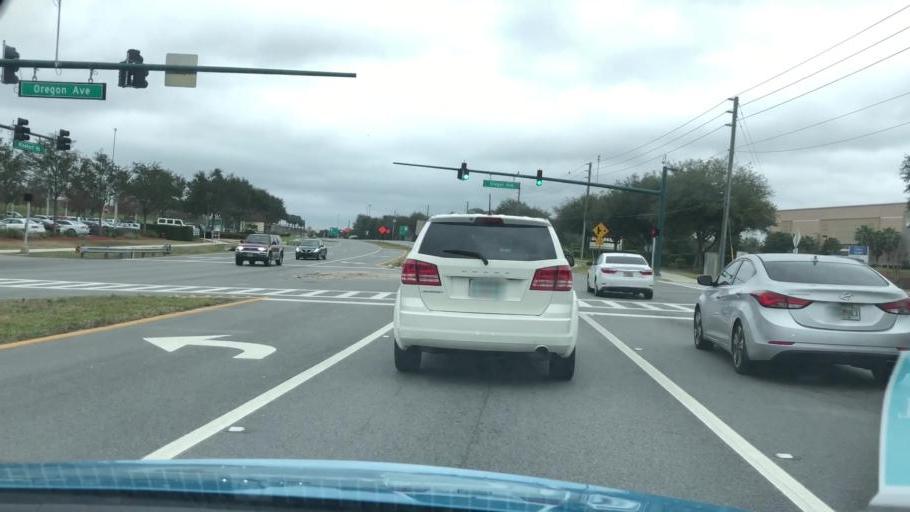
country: US
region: Florida
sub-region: Seminole County
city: Lake Mary
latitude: 28.7946
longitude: -81.3355
